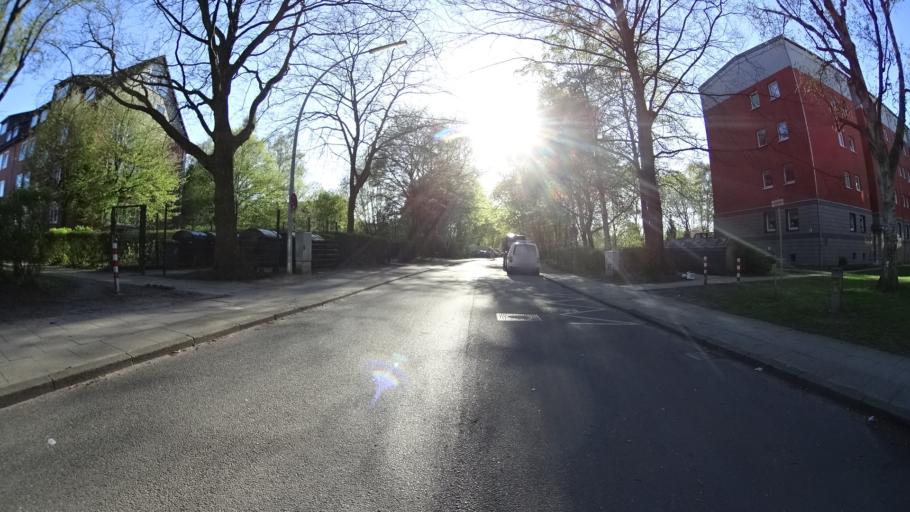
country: DE
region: Hamburg
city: Stellingen
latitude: 53.5887
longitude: 9.9373
